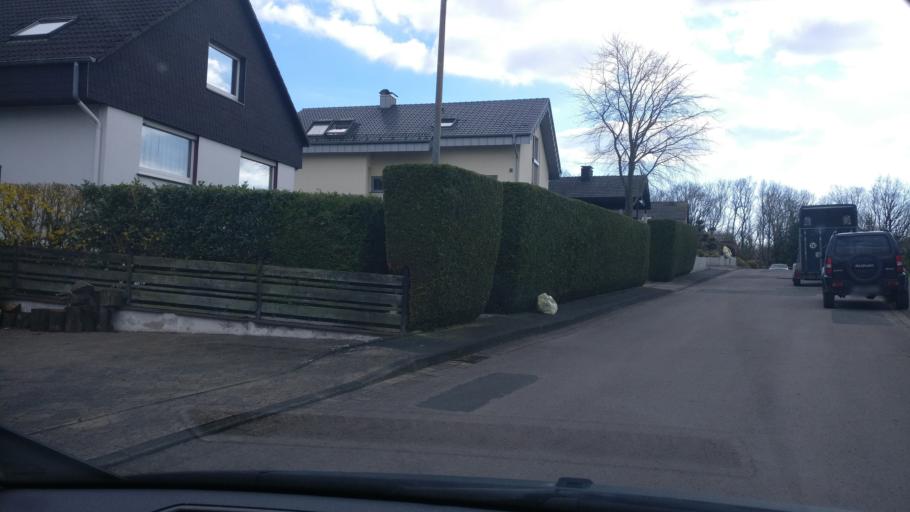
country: DE
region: North Rhine-Westphalia
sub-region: Regierungsbezirk Detmold
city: Lage
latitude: 52.0104
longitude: 8.7768
